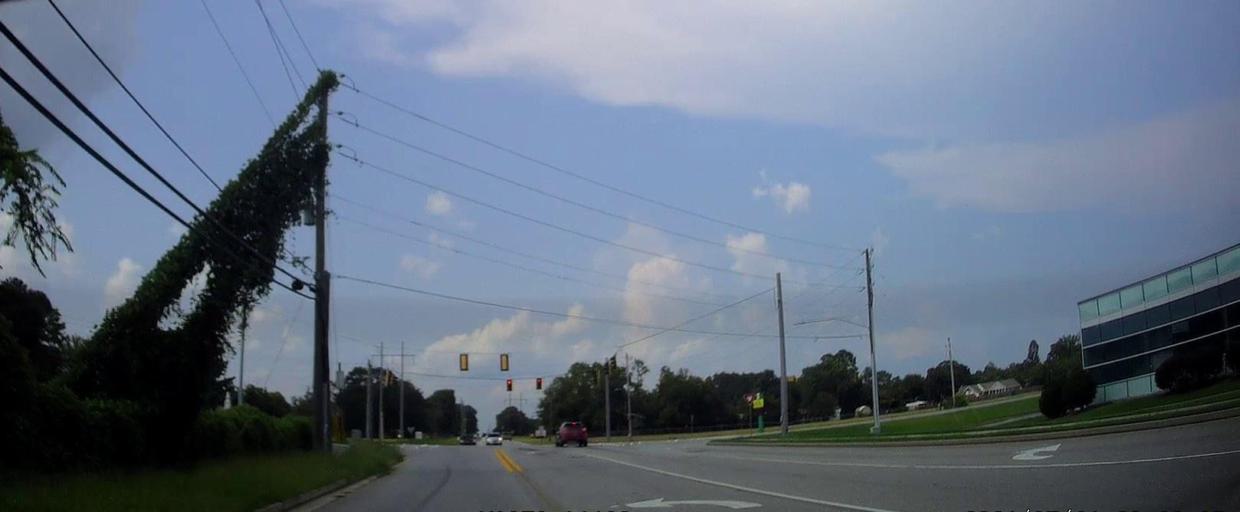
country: US
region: Georgia
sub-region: Houston County
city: Robins Air Force Base
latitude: 32.5934
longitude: -83.6031
